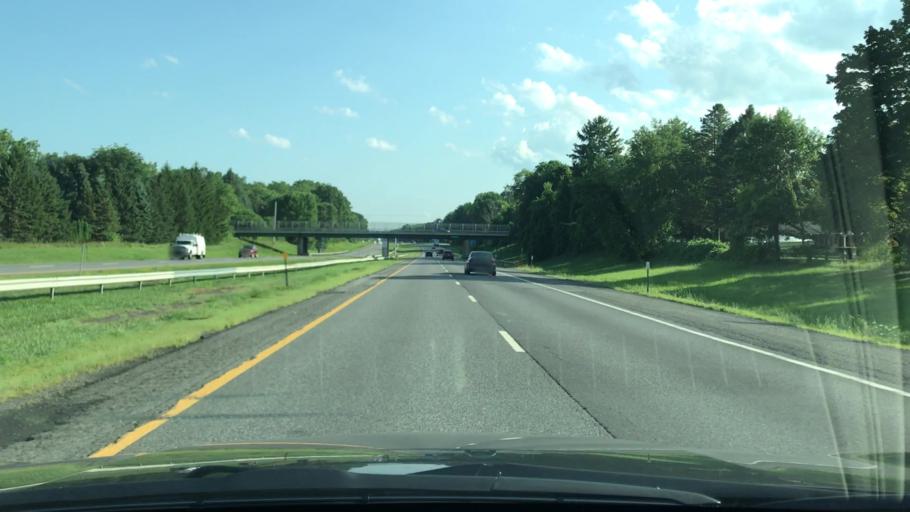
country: US
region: New York
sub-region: Albany County
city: Delmar
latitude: 42.6014
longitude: -73.7847
